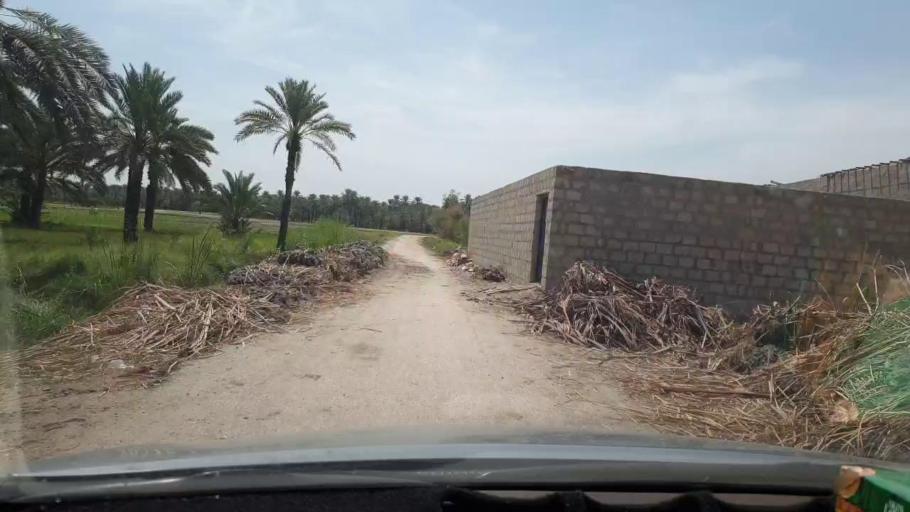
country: PK
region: Sindh
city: Khairpur
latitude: 27.4848
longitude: 68.7724
